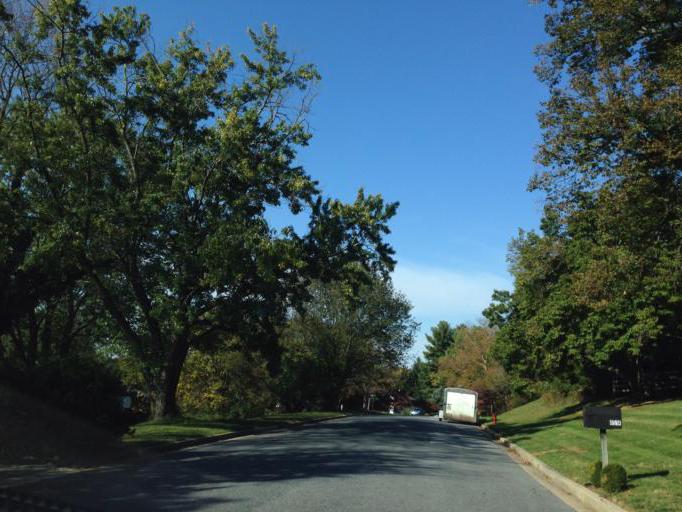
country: US
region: Maryland
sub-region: Howard County
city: Ellicott City
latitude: 39.2727
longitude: -76.8067
